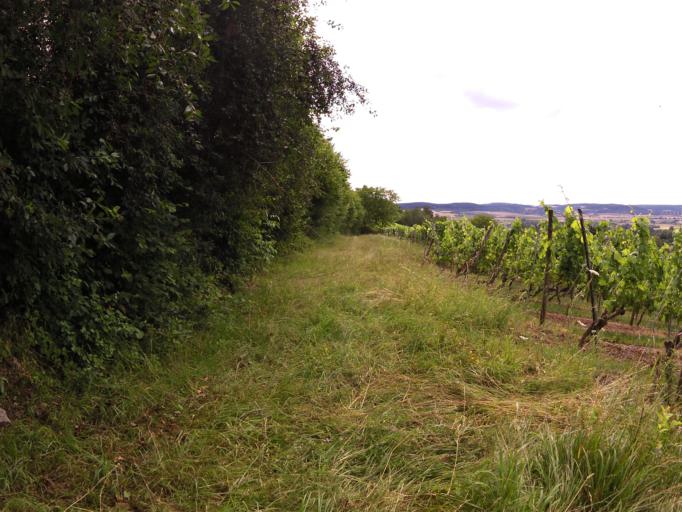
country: DE
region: Bavaria
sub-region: Regierungsbezirk Unterfranken
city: Thungersheim
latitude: 49.8869
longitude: 9.8624
